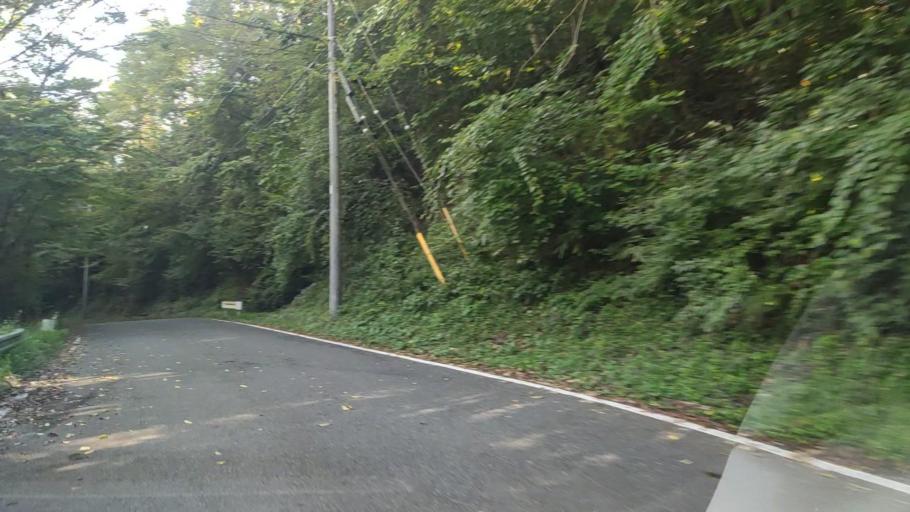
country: JP
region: Gunma
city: Nakanojomachi
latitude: 36.5961
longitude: 138.6941
